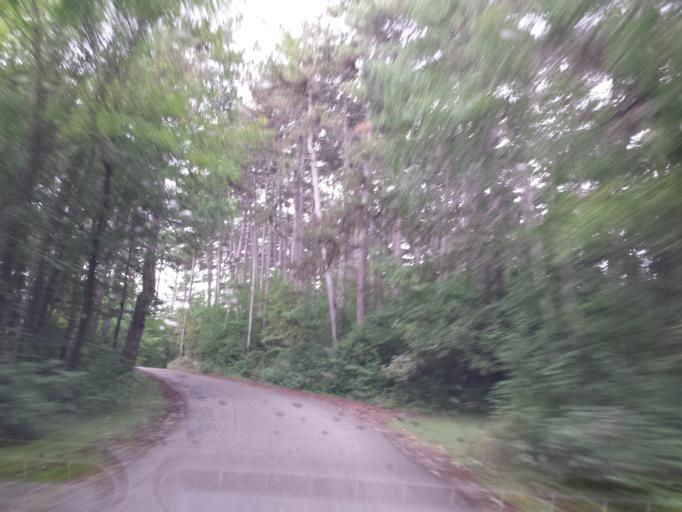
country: AT
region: Lower Austria
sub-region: Politischer Bezirk Baden
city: Hirtenberg
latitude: 47.9237
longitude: 16.1709
